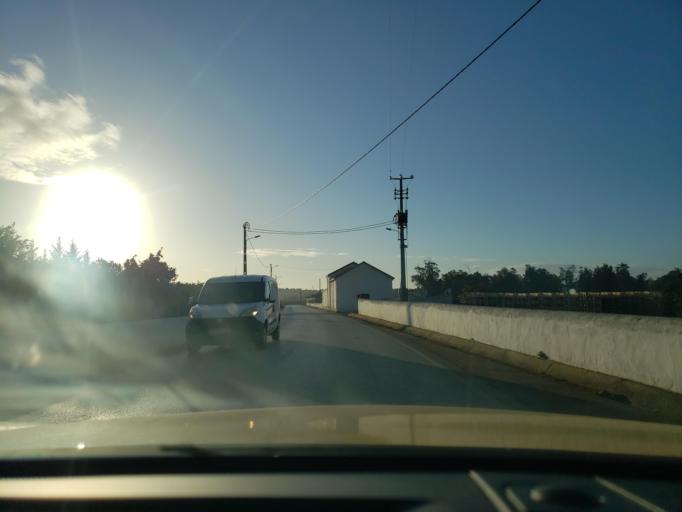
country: PT
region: Faro
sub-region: Portimao
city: Alvor
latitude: 37.1687
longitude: -8.5793
